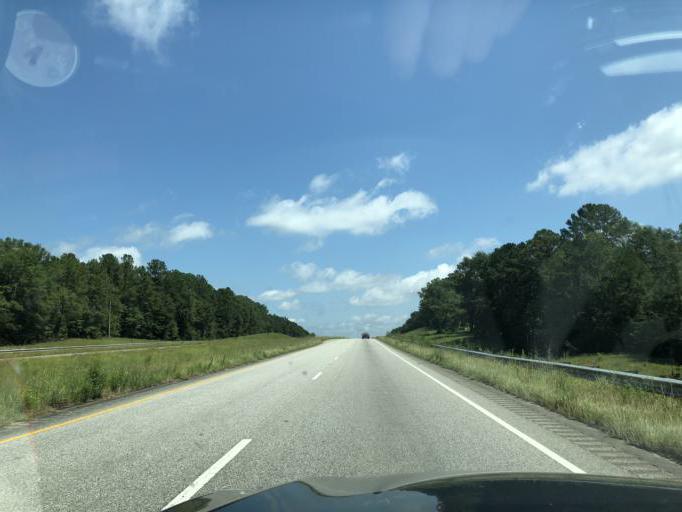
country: US
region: Alabama
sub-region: Barbour County
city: Eufaula
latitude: 31.7462
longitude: -85.2361
